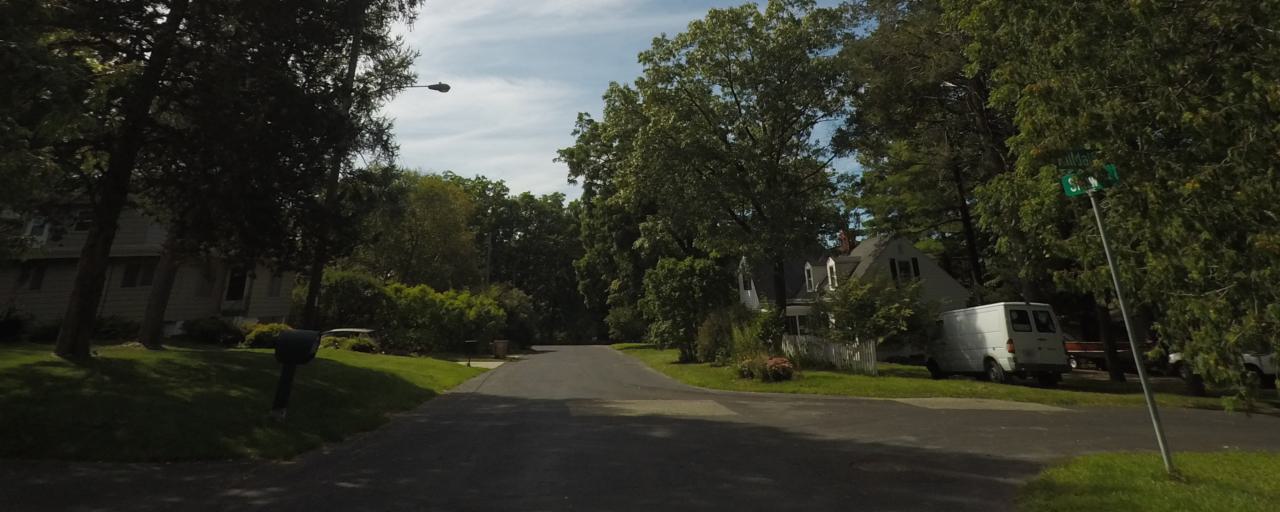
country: US
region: Wisconsin
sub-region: Dane County
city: Shorewood Hills
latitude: 43.0718
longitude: -89.4738
